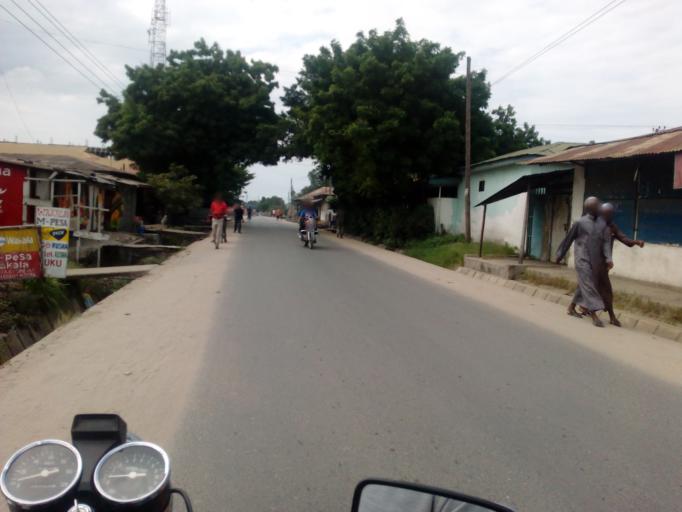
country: TZ
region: Dar es Salaam
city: Dar es Salaam
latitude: -6.8600
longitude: 39.2551
